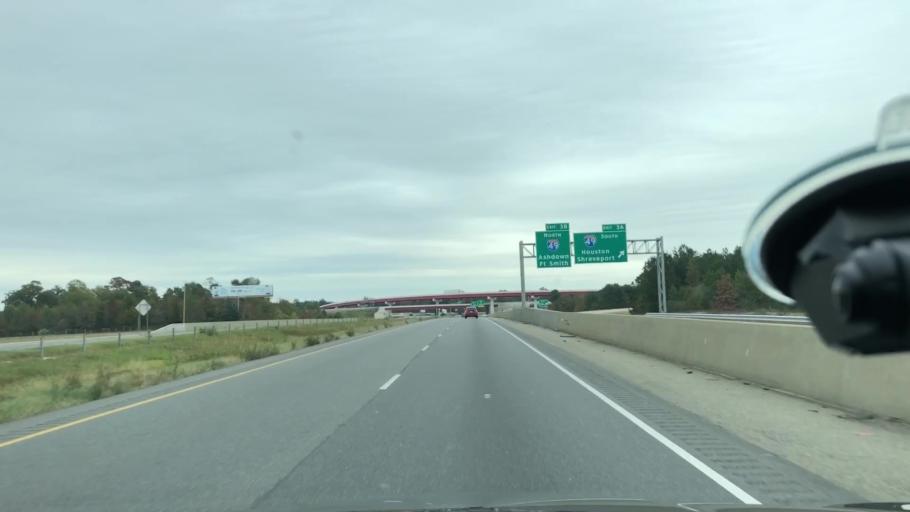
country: US
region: Arkansas
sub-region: Miller County
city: Texarkana
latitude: 33.4783
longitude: -93.9936
